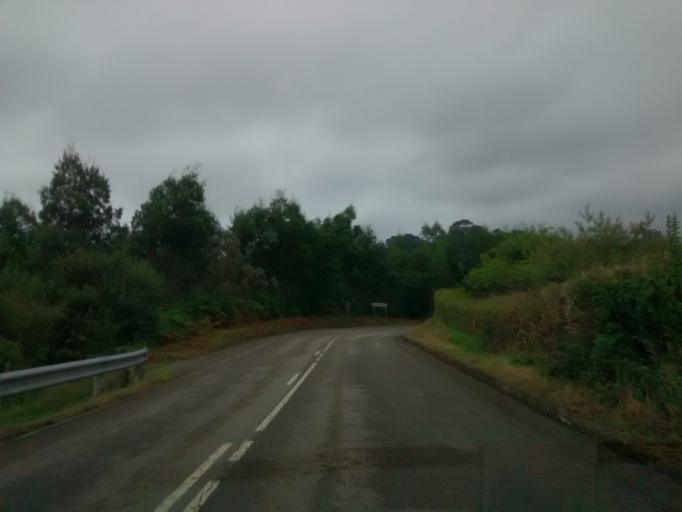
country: ES
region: Asturias
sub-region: Province of Asturias
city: Villaviciosa
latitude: 43.5355
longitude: -5.3959
